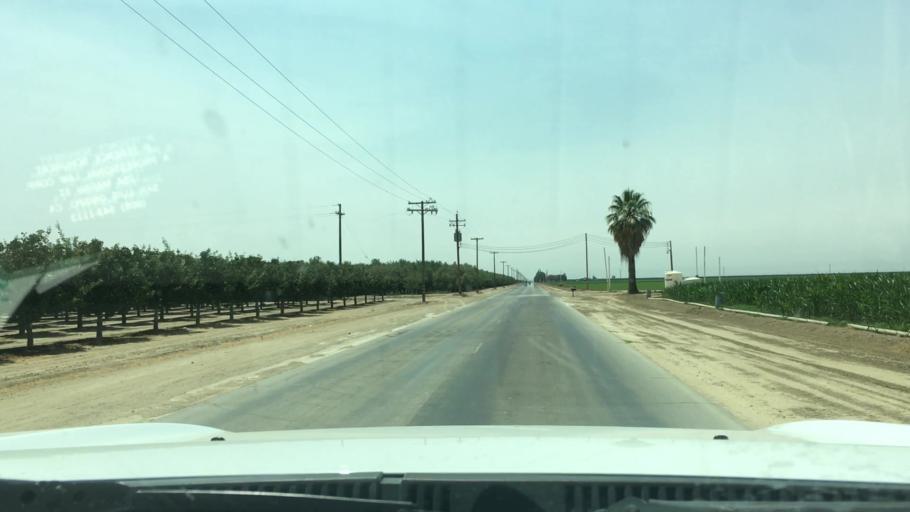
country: US
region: California
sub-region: Kern County
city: Wasco
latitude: 35.6749
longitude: -119.4374
